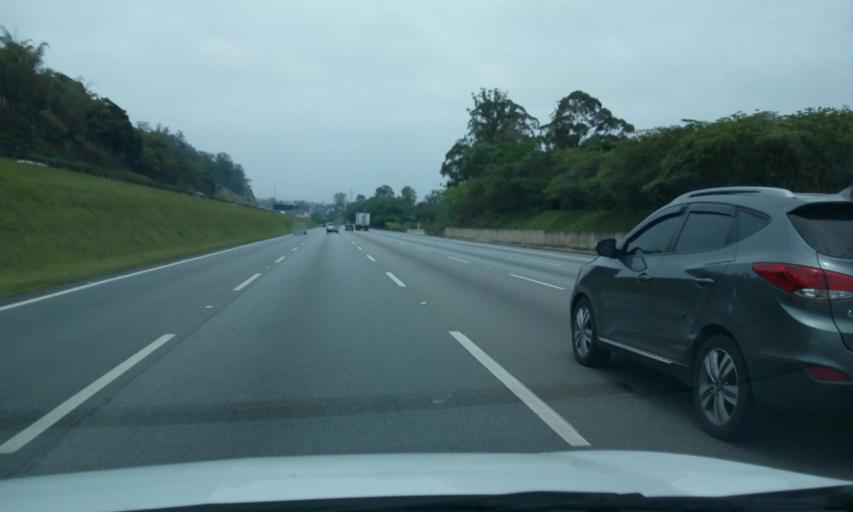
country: BR
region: Sao Paulo
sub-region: Osasco
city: Osasco
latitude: -23.4564
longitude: -46.7537
